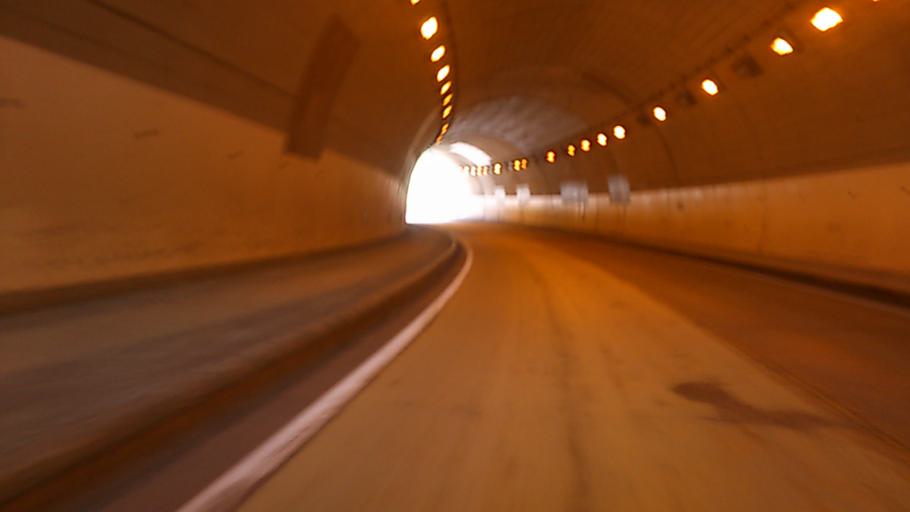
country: JP
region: Hokkaido
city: Otofuke
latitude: 43.3626
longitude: 143.2360
